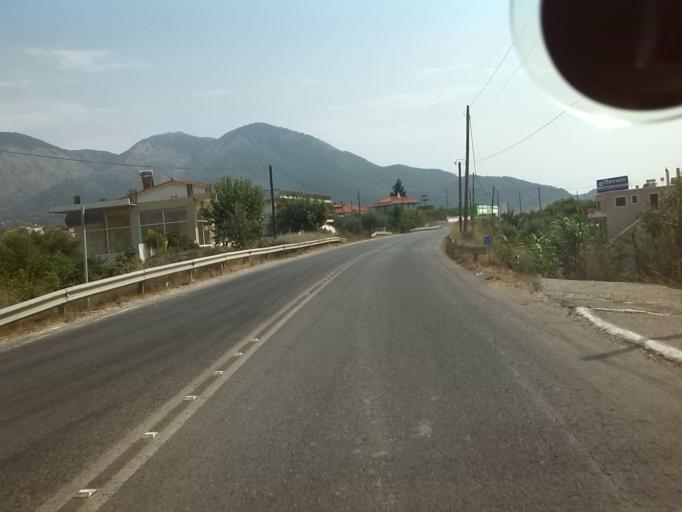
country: GR
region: Peloponnese
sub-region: Nomos Messinias
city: Kyparissia
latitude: 37.2748
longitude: 21.6984
